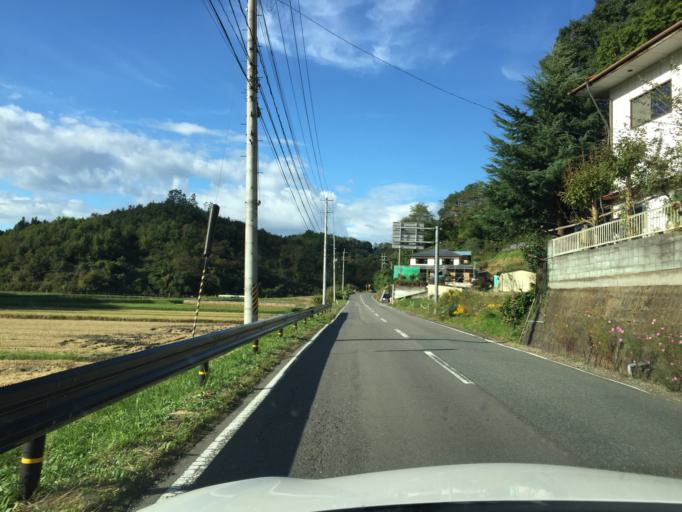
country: JP
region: Fukushima
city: Ishikawa
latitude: 37.1851
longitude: 140.4589
